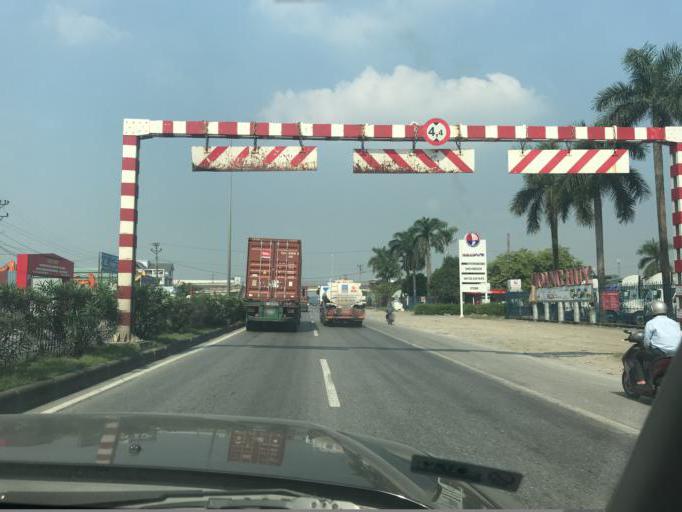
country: VN
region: Hai Phong
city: An Duong
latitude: 20.8772
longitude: 106.6145
